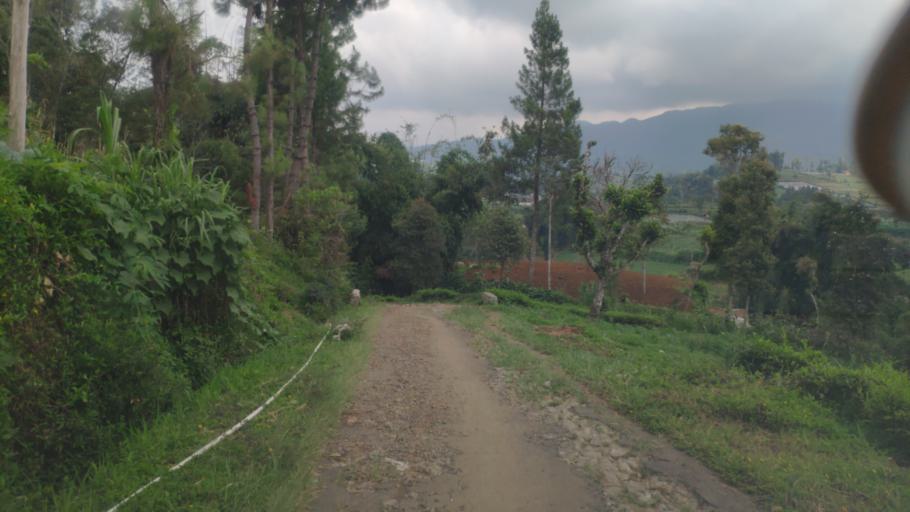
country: ID
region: Central Java
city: Wonosobo
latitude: -7.2200
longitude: 109.7553
